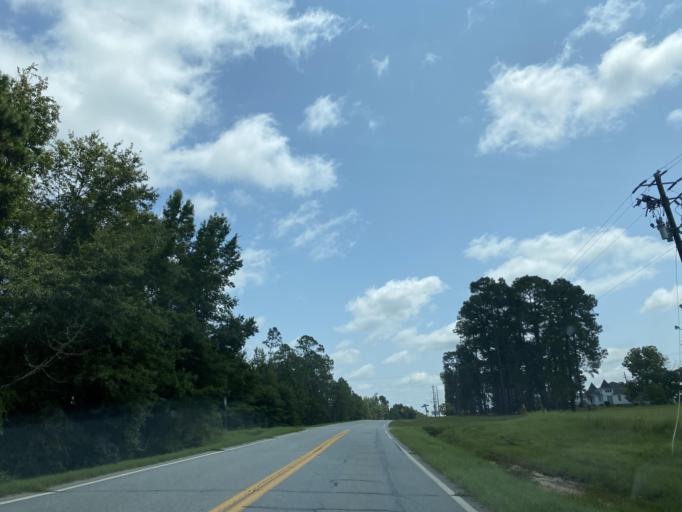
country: US
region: Georgia
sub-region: Wilcox County
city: Abbeville
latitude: 32.0082
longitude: -83.1216
